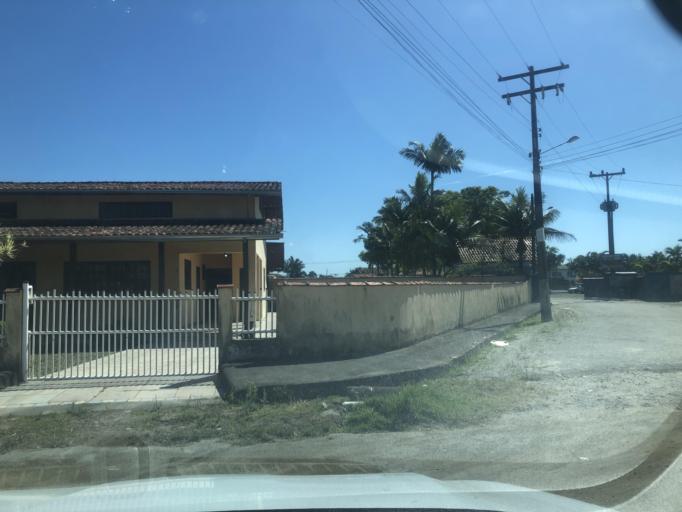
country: BR
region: Santa Catarina
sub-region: Sao Francisco Do Sul
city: Sao Francisco do Sul
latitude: -26.2150
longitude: -48.5284
